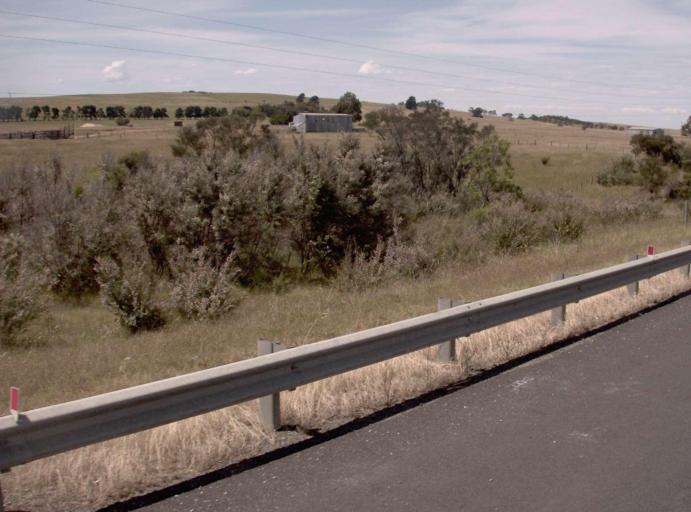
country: AU
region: Victoria
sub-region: Wellington
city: Heyfield
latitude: -38.1340
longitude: 146.8063
